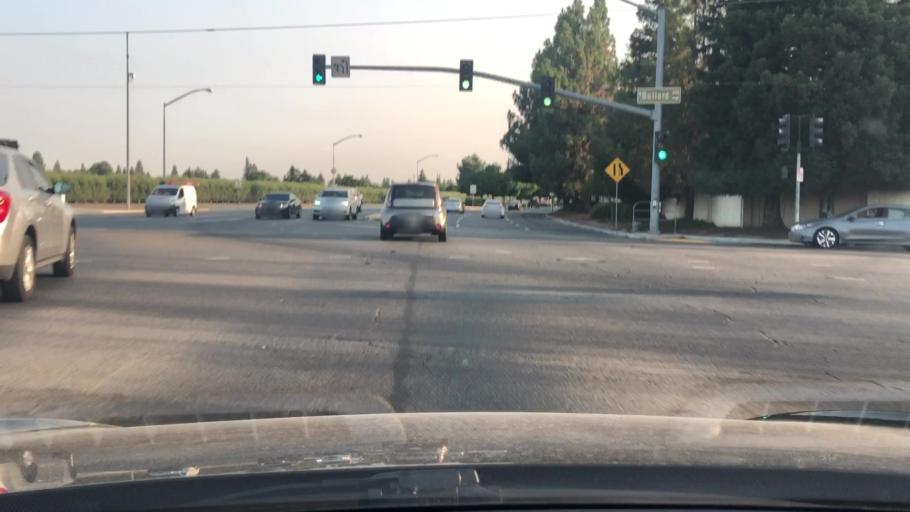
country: US
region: California
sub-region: Fresno County
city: Clovis
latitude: 36.8230
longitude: -119.7290
